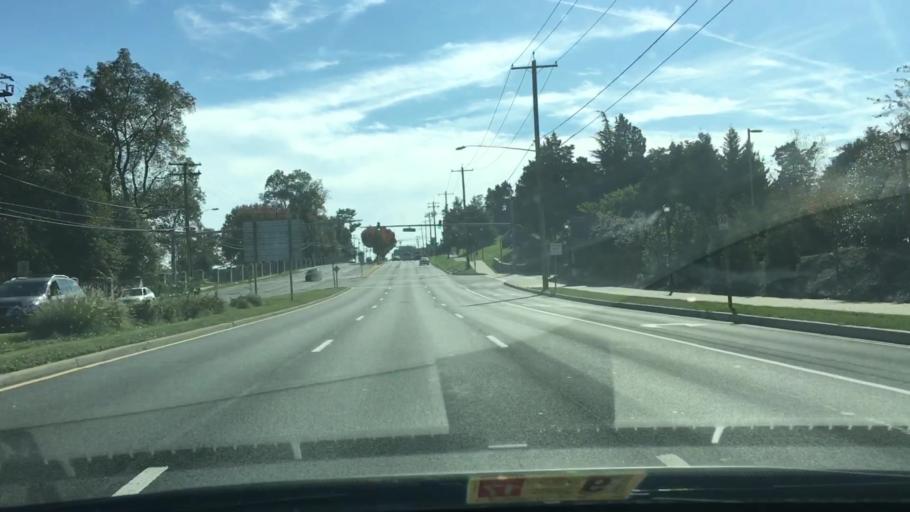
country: US
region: Maryland
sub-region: Montgomery County
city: Bethesda
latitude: 39.0033
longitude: -77.0974
